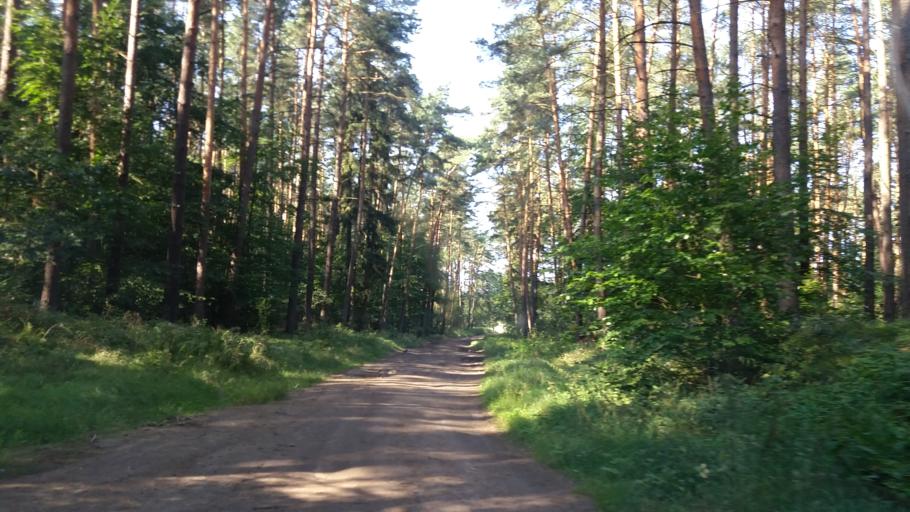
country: PL
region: West Pomeranian Voivodeship
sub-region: Powiat choszczenski
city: Pelczyce
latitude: 52.9783
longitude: 15.3536
